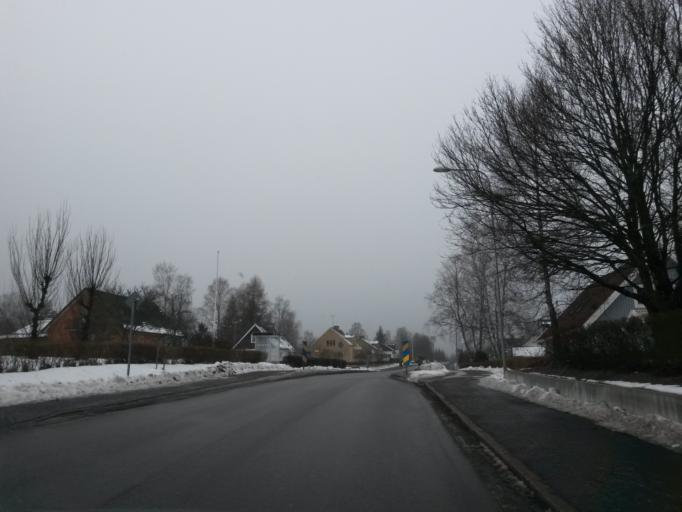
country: SE
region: Vaestra Goetaland
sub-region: Ulricehamns Kommun
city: Ulricehamn
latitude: 57.6661
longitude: 13.4259
